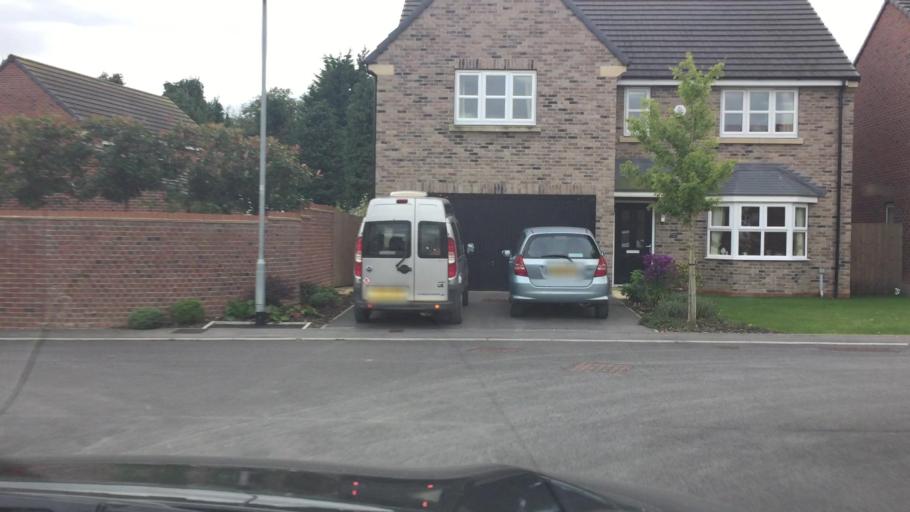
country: GB
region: England
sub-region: East Riding of Yorkshire
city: Pocklington
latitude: 53.9243
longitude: -0.7817
